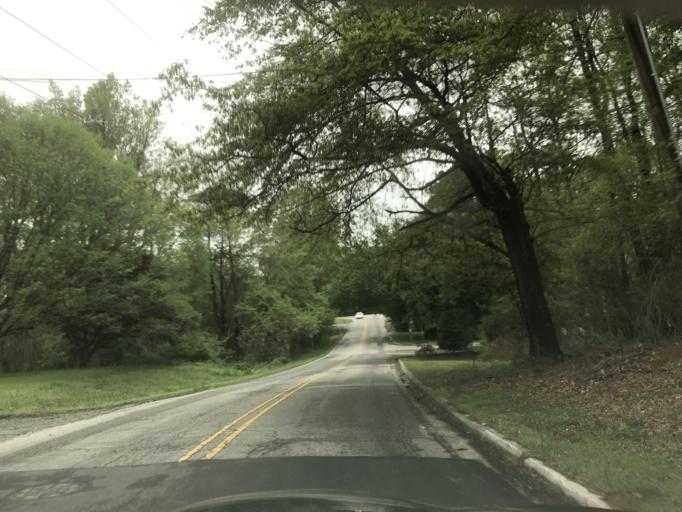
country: US
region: North Carolina
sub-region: Wake County
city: Raleigh
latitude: 35.7519
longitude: -78.6662
